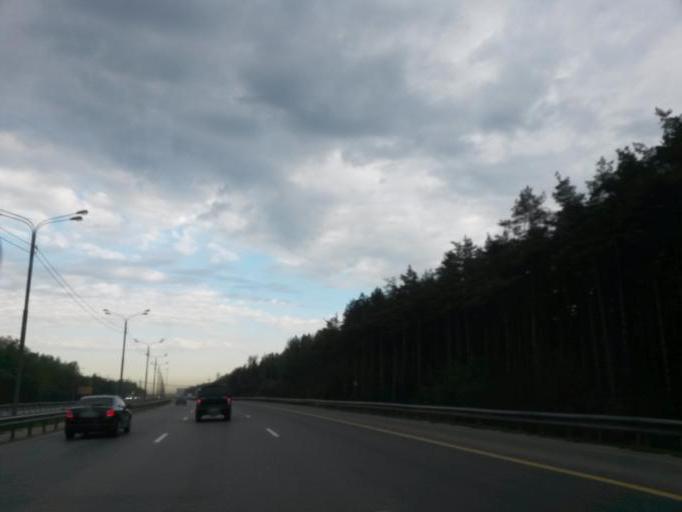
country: RU
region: Moskovskaya
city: Domodedovo
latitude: 55.4513
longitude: 37.7894
